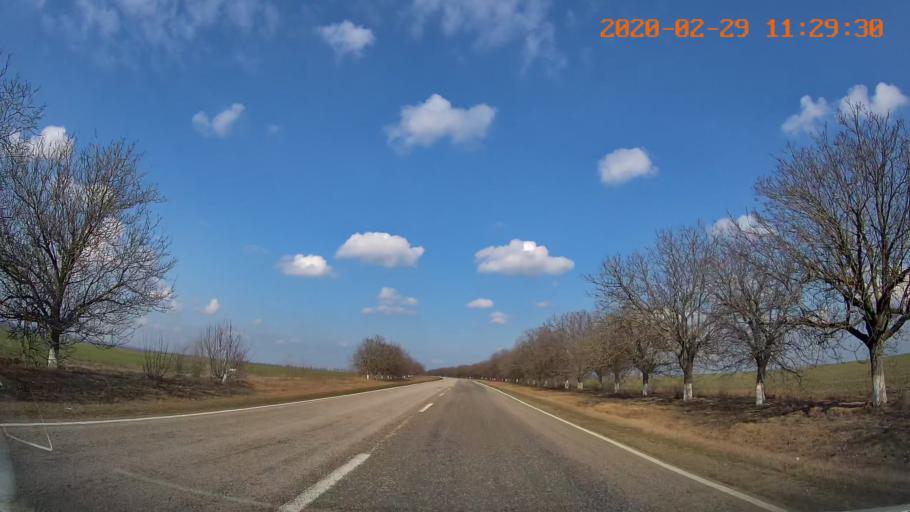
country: MD
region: Telenesti
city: Cocieri
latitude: 47.4955
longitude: 29.1250
